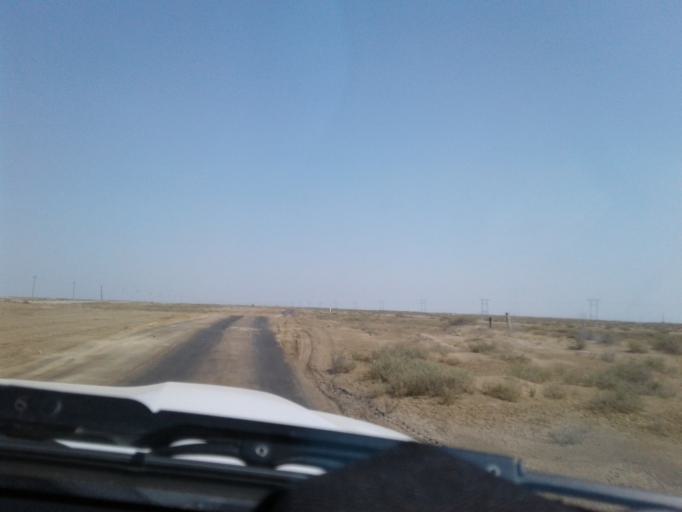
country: IR
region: Golestan
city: Gomishan
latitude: 37.7867
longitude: 53.9174
